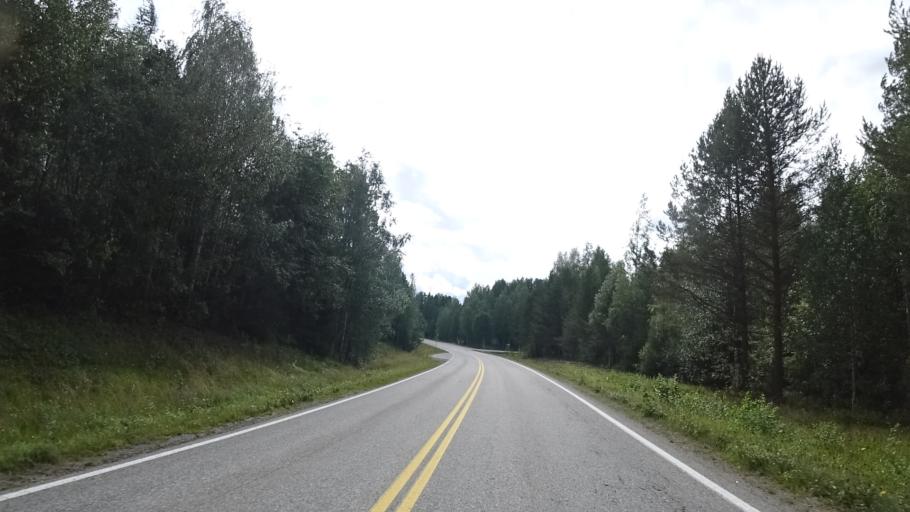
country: FI
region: North Karelia
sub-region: Joensuu
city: Ilomantsi
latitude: 62.7540
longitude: 30.9997
